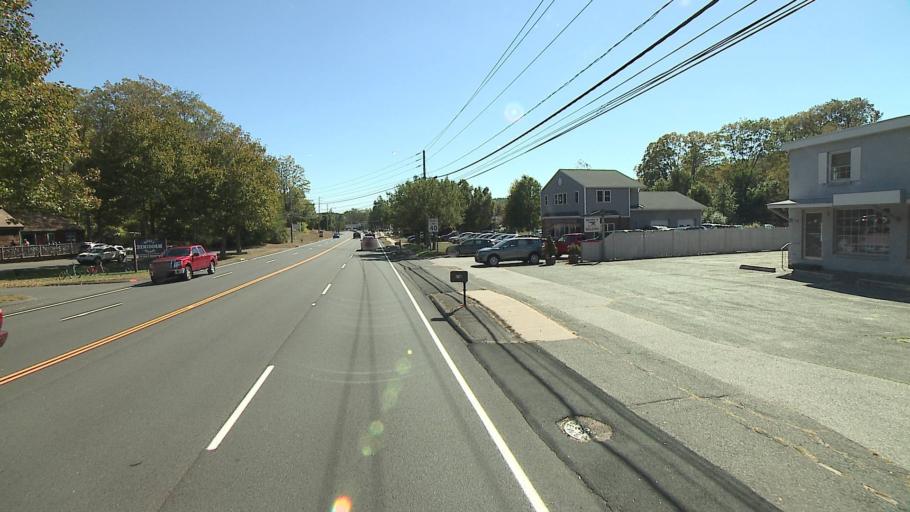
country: US
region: Connecticut
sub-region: Hartford County
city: Canton Valley
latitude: 41.8284
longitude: -72.9006
